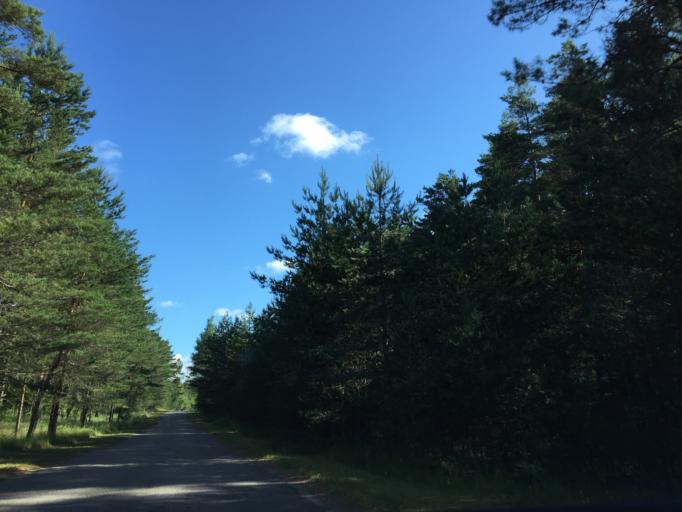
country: LV
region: Ventspils
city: Ventspils
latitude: 57.4508
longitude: 21.6270
